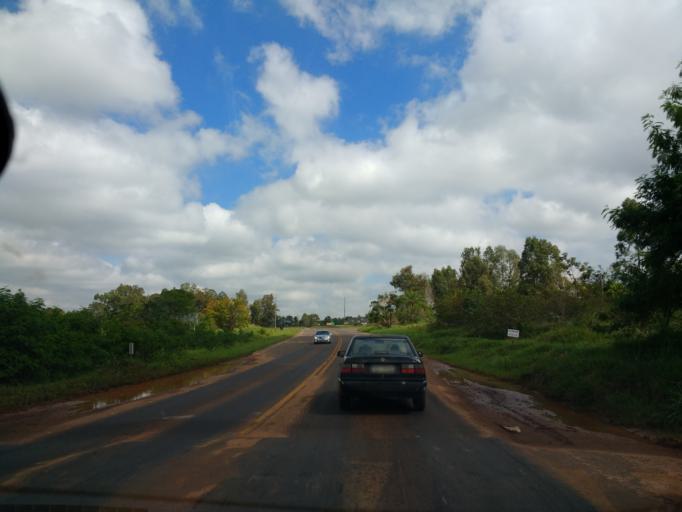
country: BR
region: Parana
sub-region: Cruzeiro Do Oeste
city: Cruzeiro do Oeste
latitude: -23.7938
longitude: -53.0453
